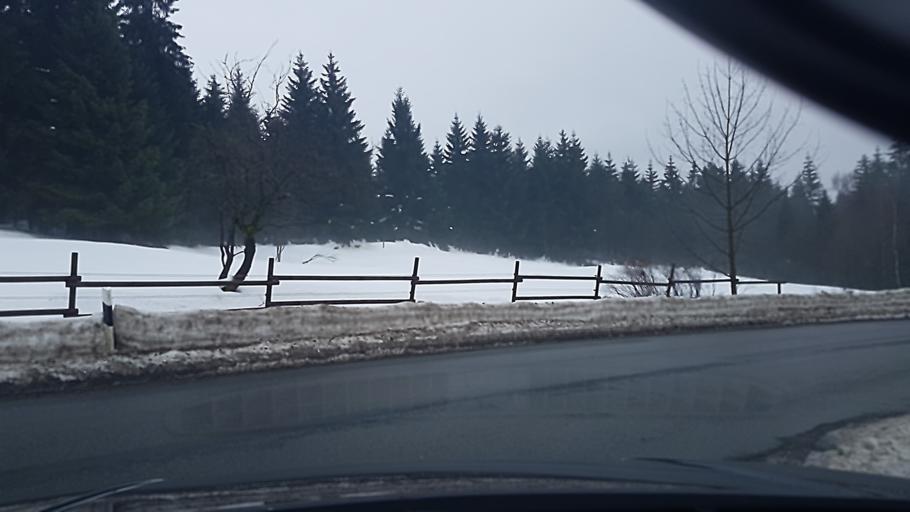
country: DE
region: Lower Saxony
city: Clausthal-Zellerfeld
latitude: 51.8472
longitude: 10.3311
